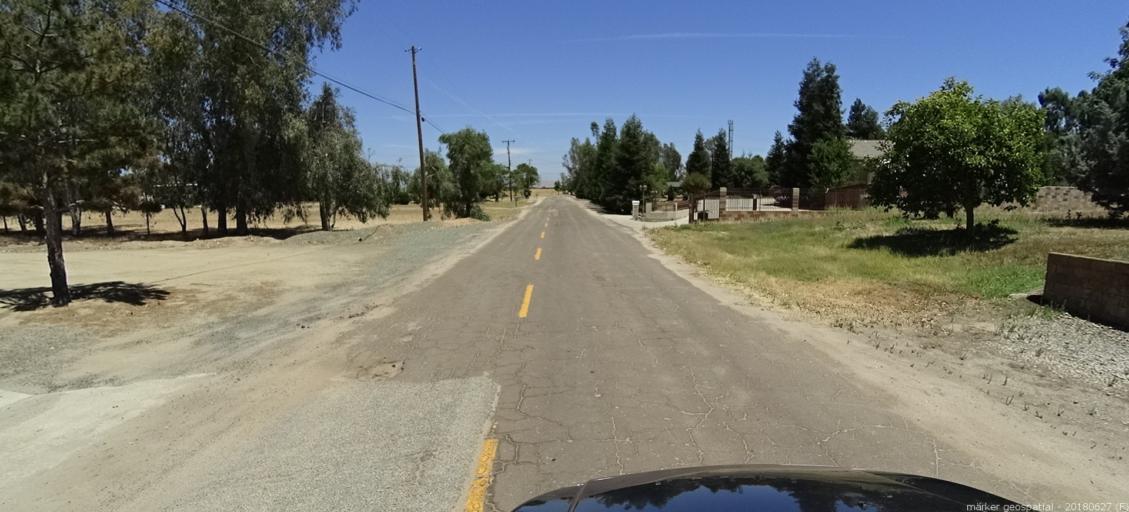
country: US
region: California
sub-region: Madera County
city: Bonadelle Ranchos-Madera Ranchos
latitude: 36.9279
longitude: -119.8612
